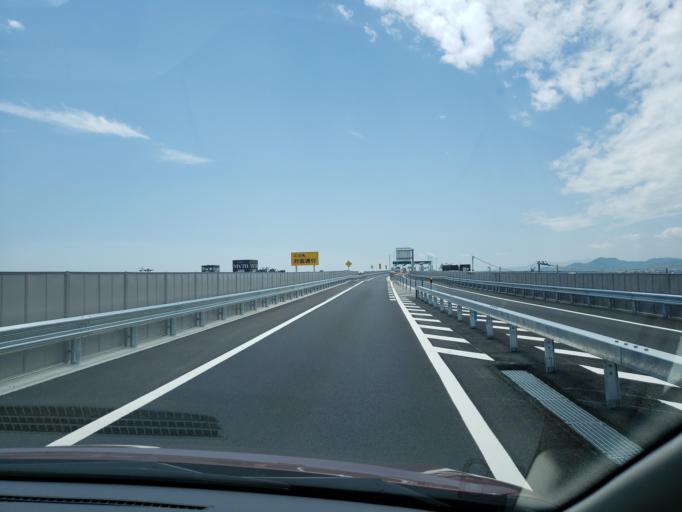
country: JP
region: Tokushima
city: Tokushima-shi
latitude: 34.0893
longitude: 134.6012
